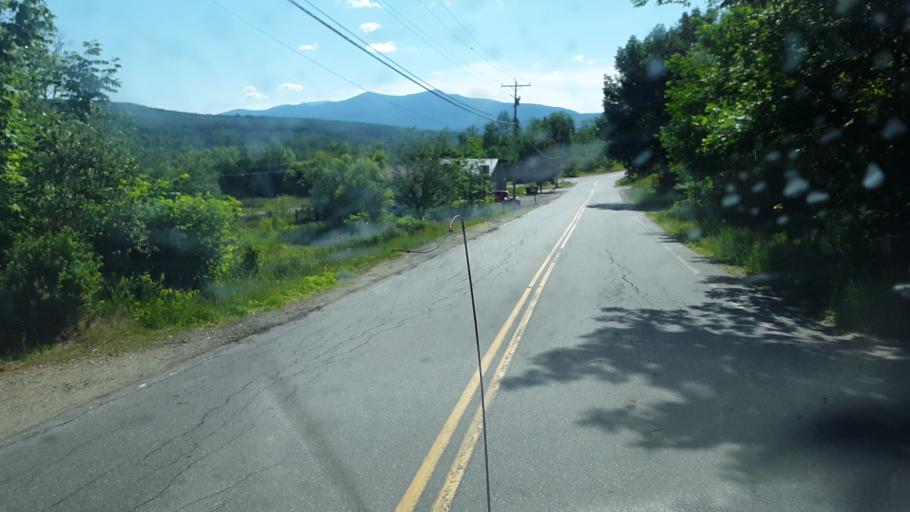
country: US
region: New Hampshire
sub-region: Grafton County
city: North Haverhill
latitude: 44.1033
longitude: -71.9033
